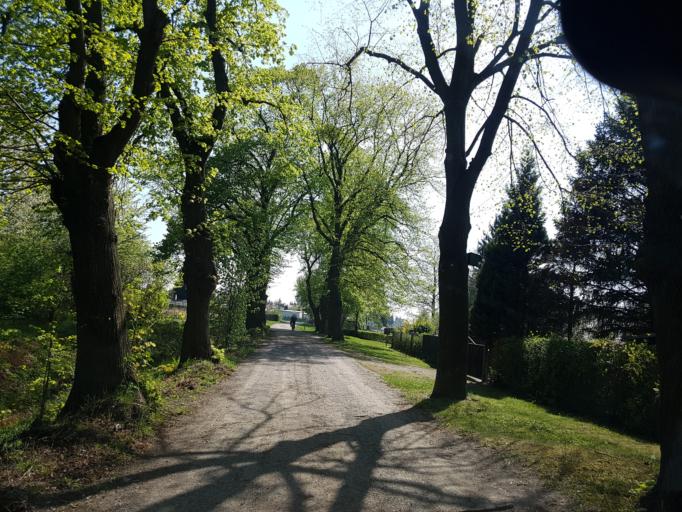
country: DE
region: Brandenburg
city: Finsterwalde
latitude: 51.6270
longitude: 13.6942
